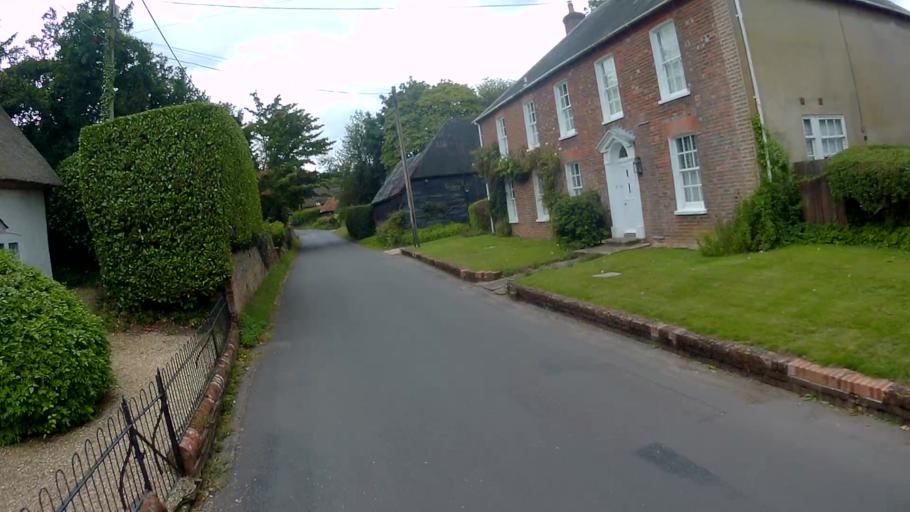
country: GB
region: England
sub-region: Hampshire
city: Basingstoke
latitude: 51.2127
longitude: -1.1589
